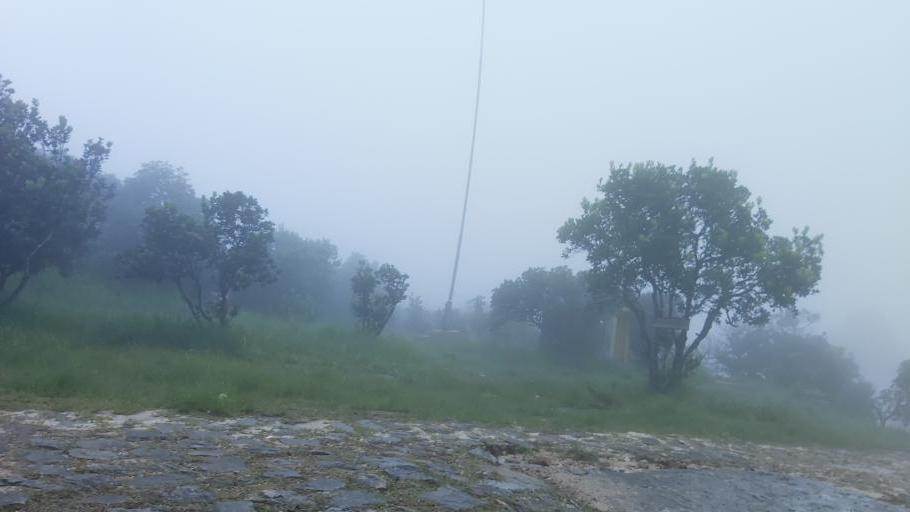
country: KH
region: Kampot
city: Kampot
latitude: 10.6297
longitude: 104.0179
